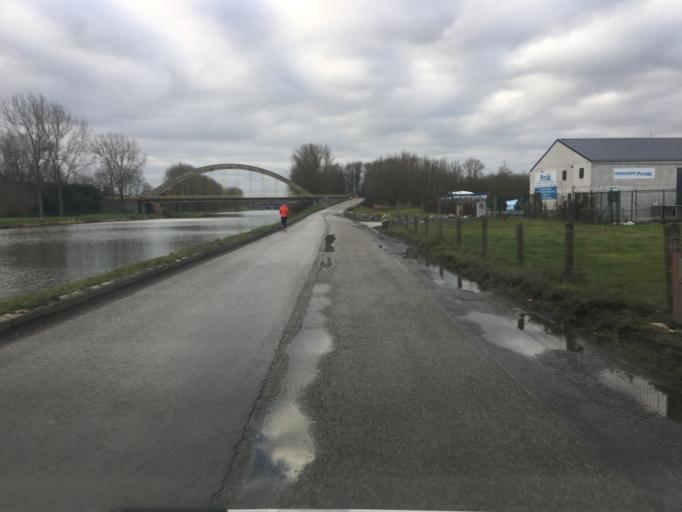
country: BE
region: Wallonia
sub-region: Province du Hainaut
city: Manage
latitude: 50.5107
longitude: 4.2108
